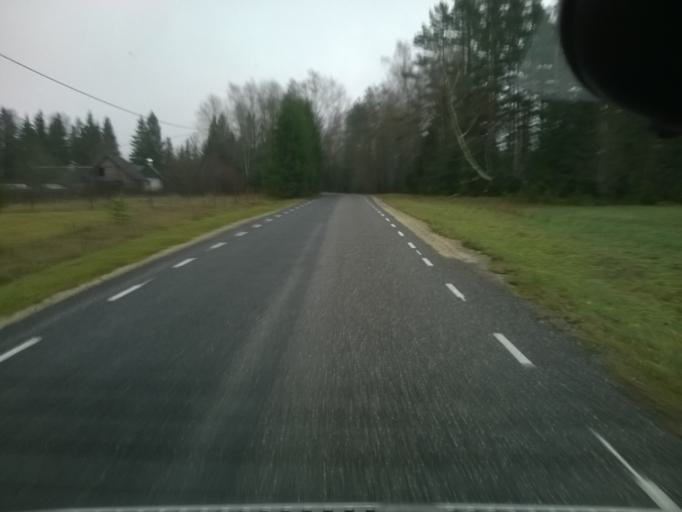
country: EE
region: Harju
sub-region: Saue linn
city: Saue
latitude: 59.1432
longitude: 24.5600
